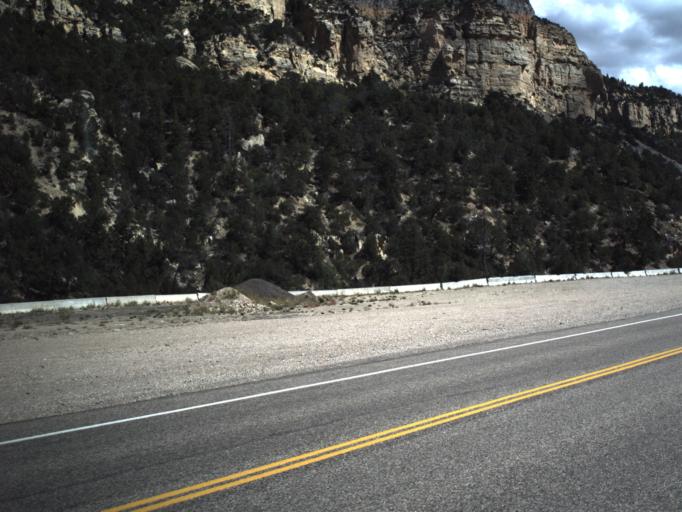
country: US
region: Utah
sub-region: Iron County
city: Cedar City
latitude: 37.6347
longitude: -112.9454
